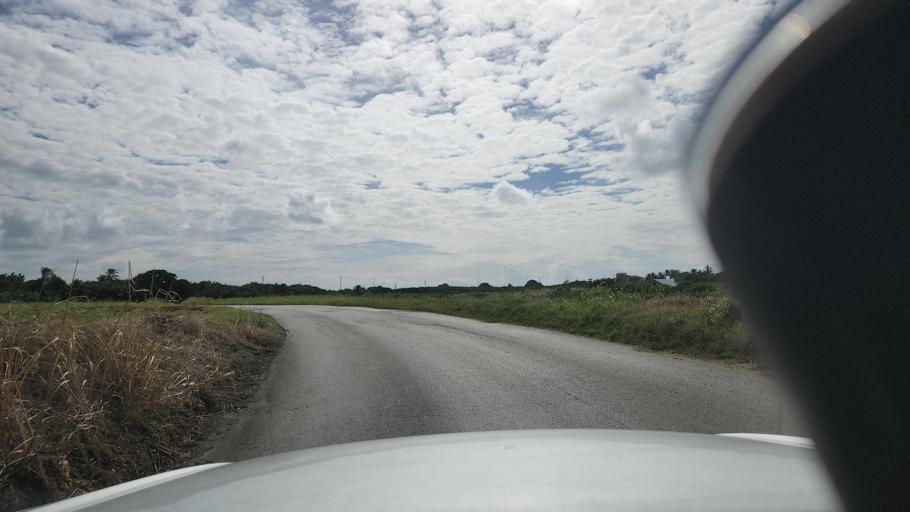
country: BB
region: Saint Lucy
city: Checker Hall
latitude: 13.2846
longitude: -59.6302
